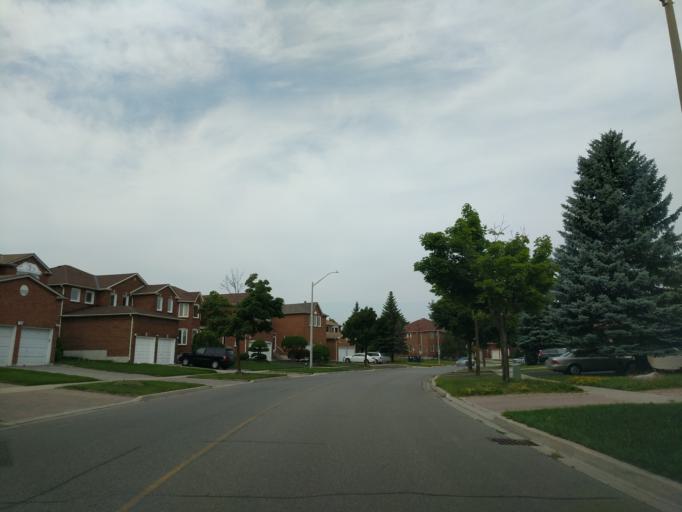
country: CA
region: Ontario
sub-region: York
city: Richmond Hill
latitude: 43.8452
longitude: -79.3981
